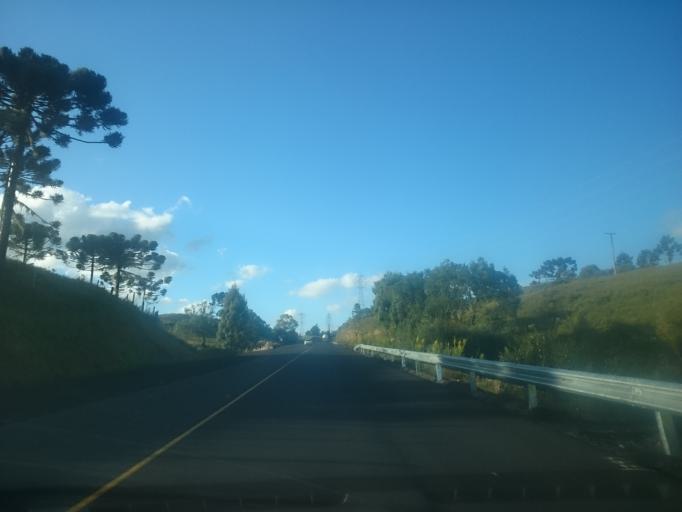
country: BR
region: Santa Catarina
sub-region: Sao Joaquim
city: Sao Joaquim
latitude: -28.0599
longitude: -50.0737
